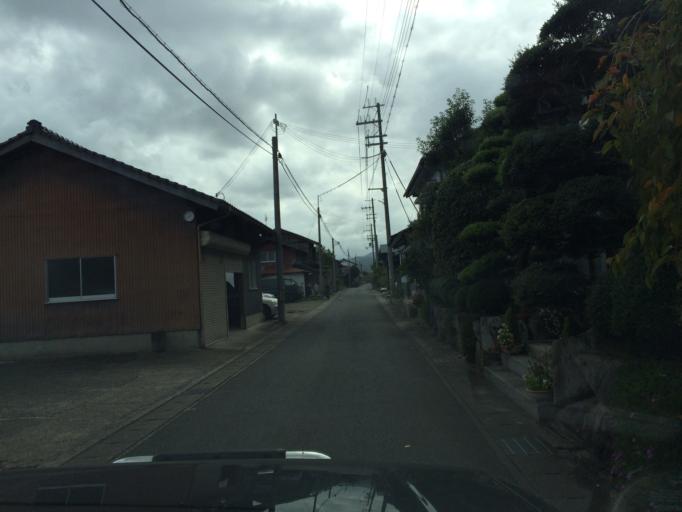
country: JP
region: Hyogo
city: Toyooka
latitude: 35.5068
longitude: 134.8110
